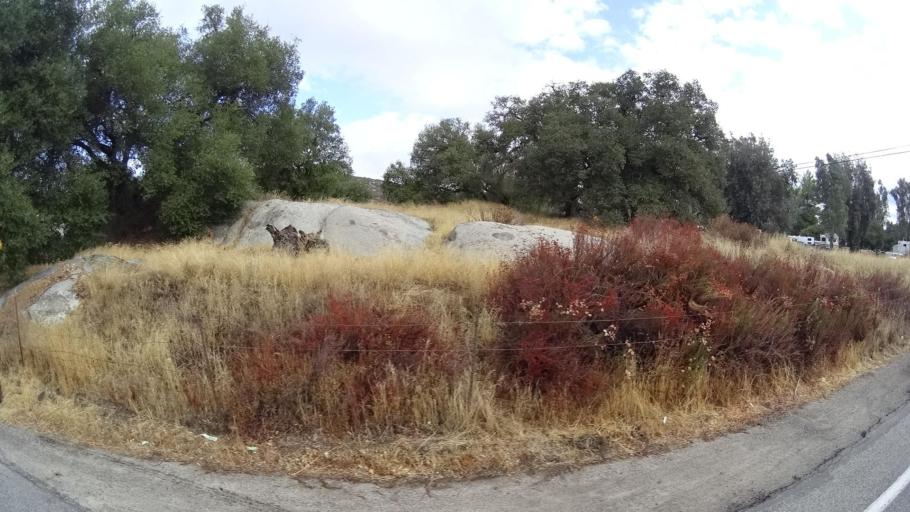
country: MX
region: Baja California
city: Tecate
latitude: 32.6231
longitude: -116.6138
